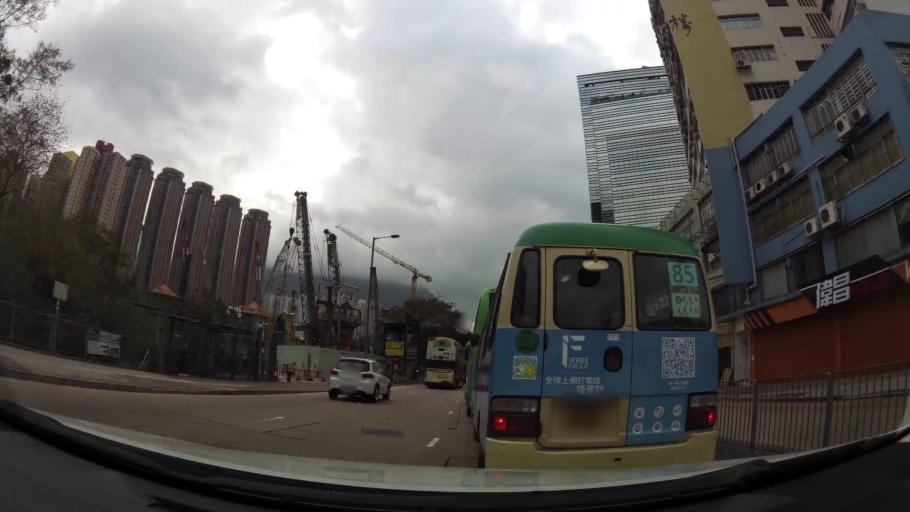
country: HK
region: Wong Tai Sin
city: Wong Tai Sin
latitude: 22.3394
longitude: 114.1986
